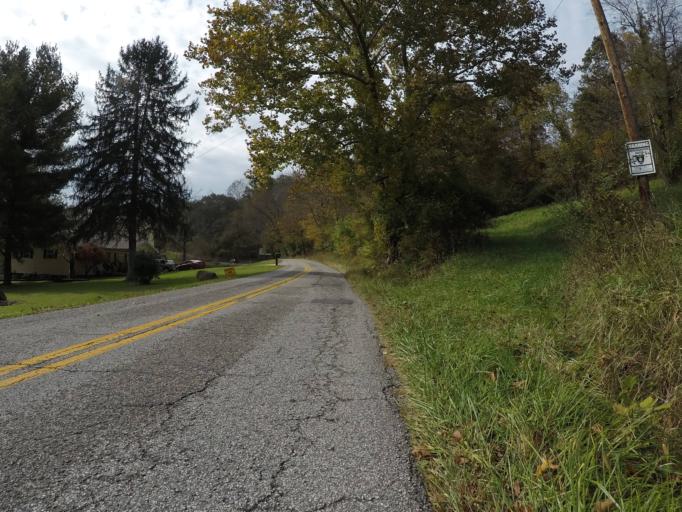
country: US
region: West Virginia
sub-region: Cabell County
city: Huntington
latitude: 38.3779
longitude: -82.4034
